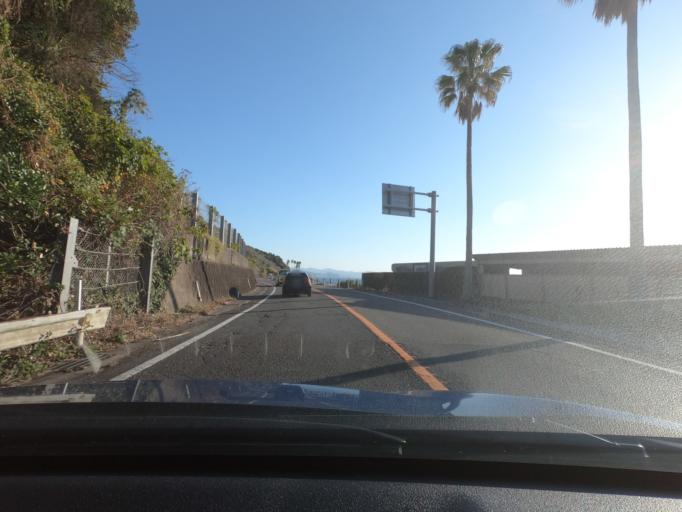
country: JP
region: Kagoshima
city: Akune
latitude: 31.9656
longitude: 130.2122
